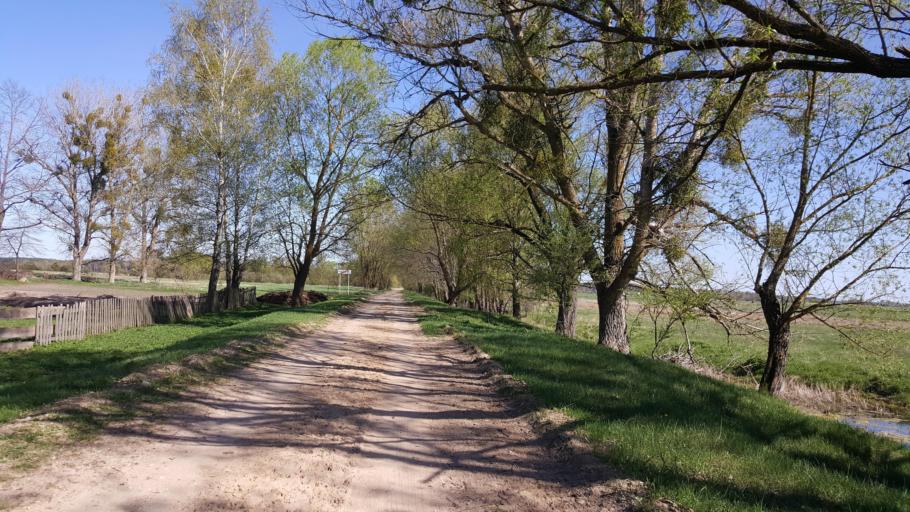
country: BY
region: Brest
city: Kamyanyets
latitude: 52.4239
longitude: 23.8732
